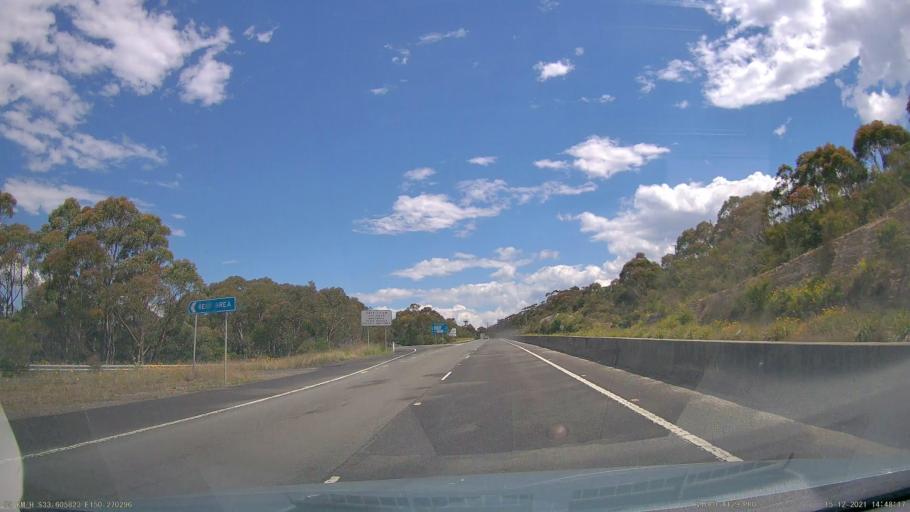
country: AU
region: New South Wales
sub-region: Blue Mountains Municipality
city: Blackheath
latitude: -33.6060
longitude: 150.2703
